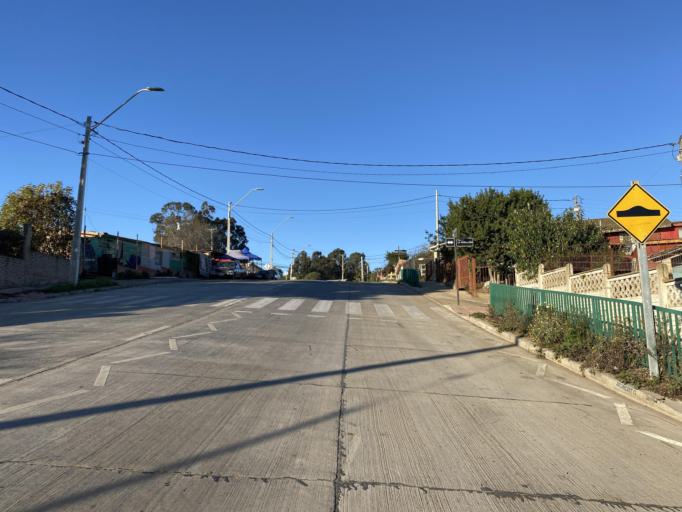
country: CL
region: Valparaiso
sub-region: San Antonio Province
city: Cartagena
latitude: -33.5505
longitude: -71.5909
